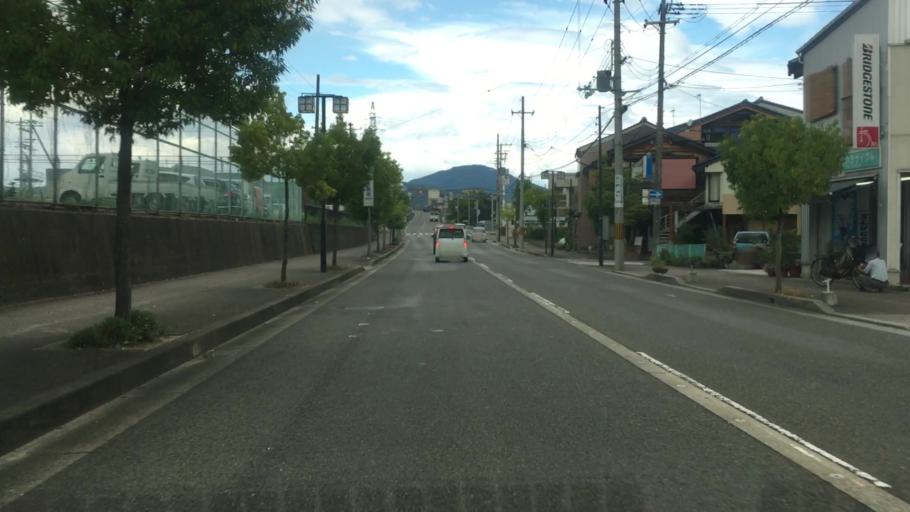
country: JP
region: Hyogo
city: Toyooka
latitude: 35.5456
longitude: 134.8137
